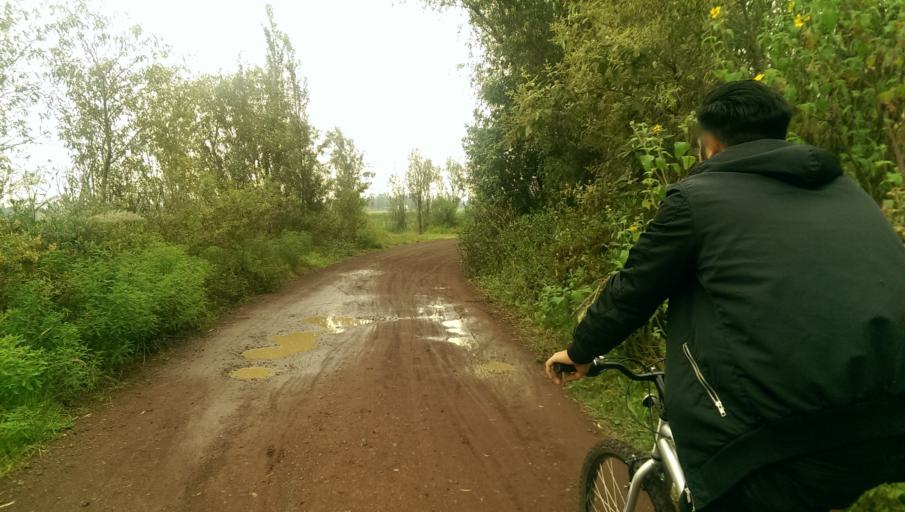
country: MX
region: Mexico City
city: Xochimilco
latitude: 19.2753
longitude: -99.0768
